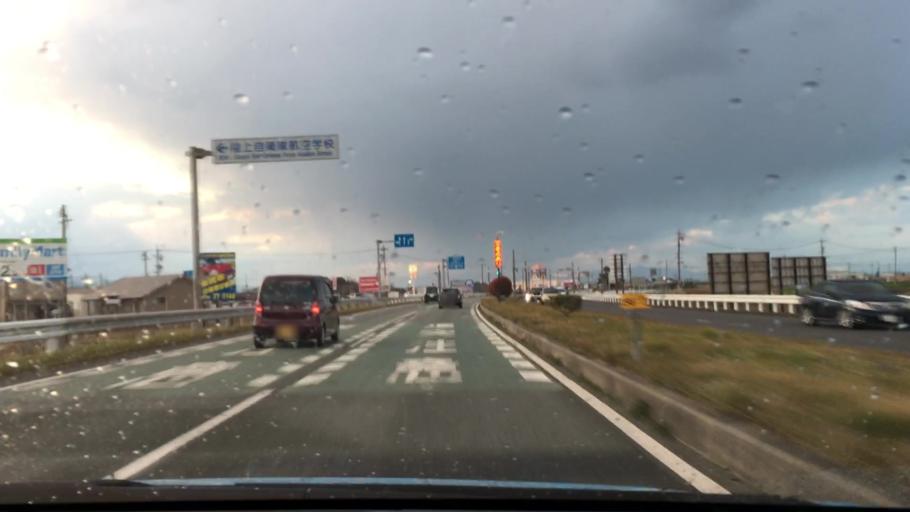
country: JP
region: Mie
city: Ise
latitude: 34.5414
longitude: 136.6649
